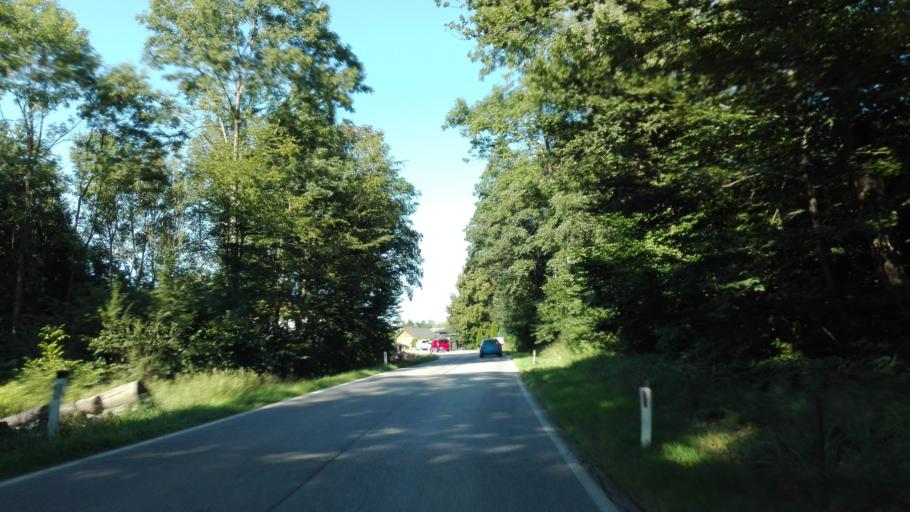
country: AT
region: Lower Austria
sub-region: Politischer Bezirk Sankt Polten
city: Eichgraben
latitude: 48.1569
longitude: 15.9666
